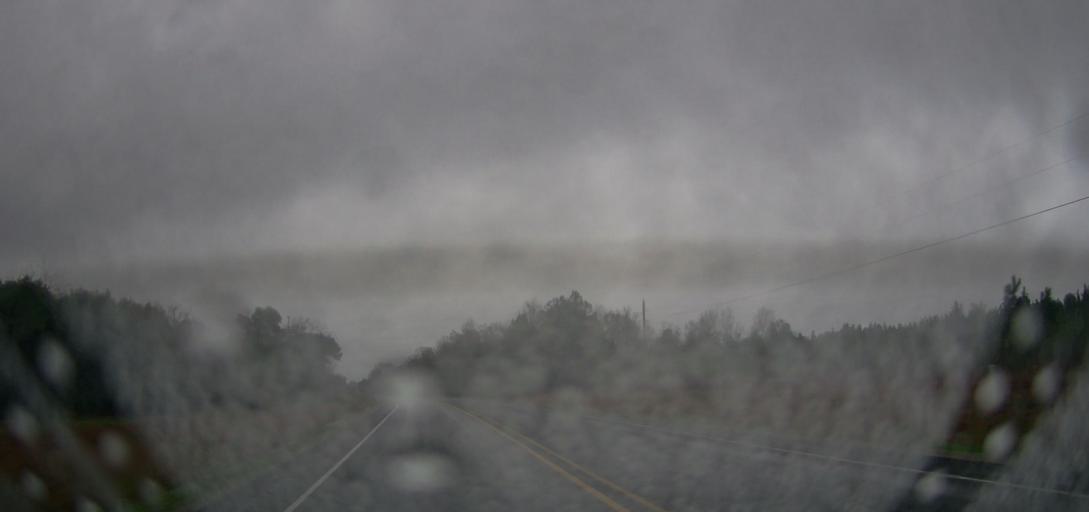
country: US
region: Alabama
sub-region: Chilton County
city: Clanton
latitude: 32.6461
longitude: -86.7622
